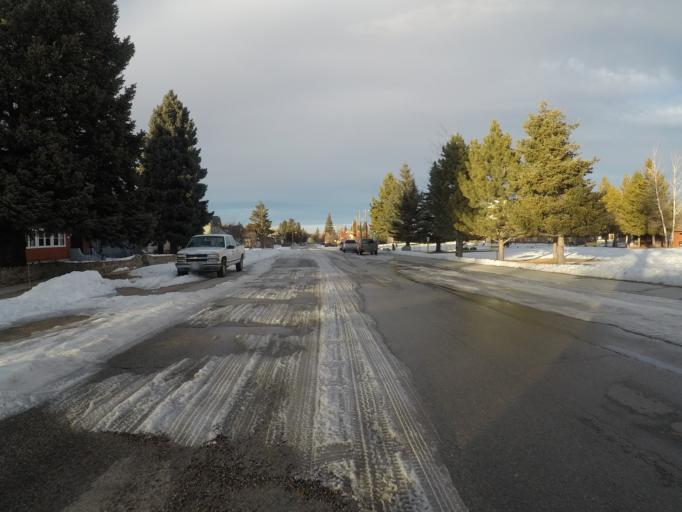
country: US
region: Montana
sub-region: Carbon County
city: Red Lodge
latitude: 45.1901
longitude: -109.2484
